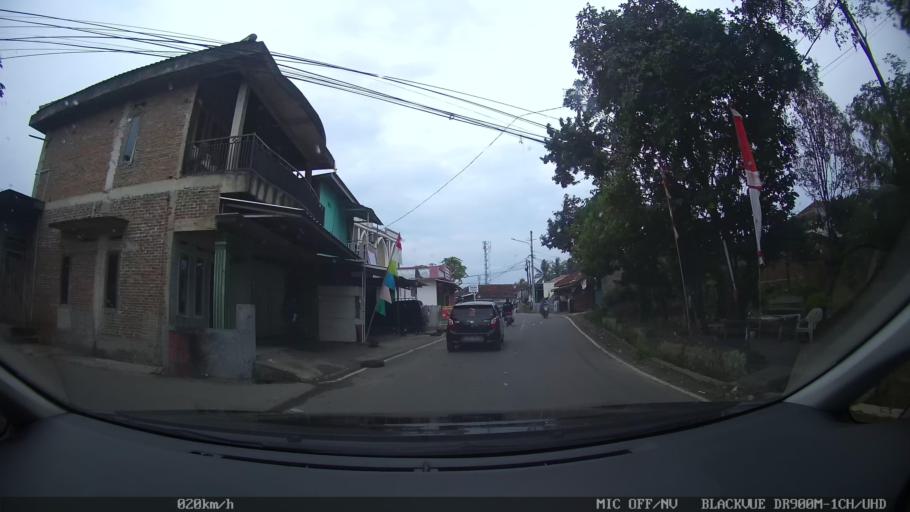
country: ID
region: Lampung
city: Kedaton
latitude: -5.3794
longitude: 105.2422
